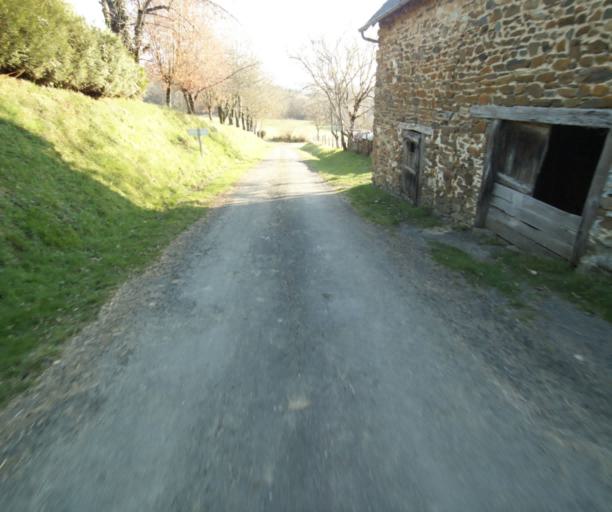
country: FR
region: Limousin
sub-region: Departement de la Correze
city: Saint-Clement
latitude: 45.3522
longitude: 1.6738
